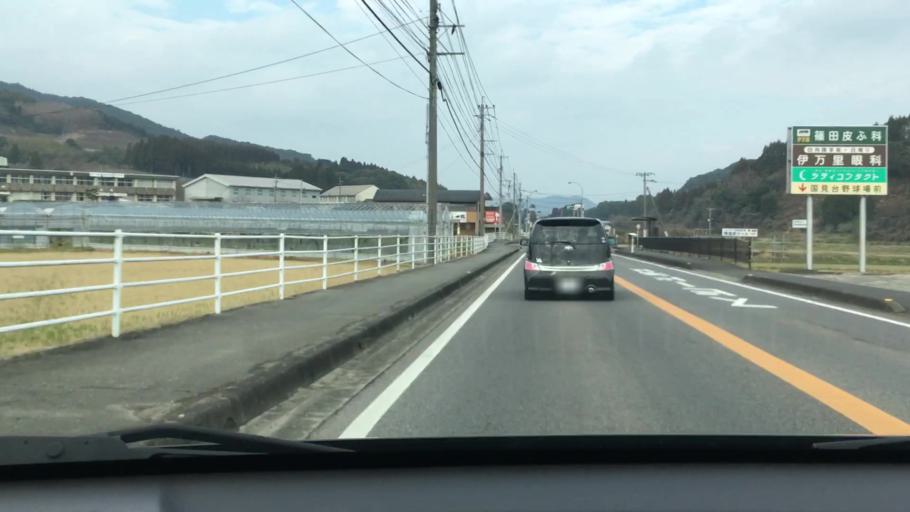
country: JP
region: Saga Prefecture
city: Imaricho-ko
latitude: 33.3157
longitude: 129.9288
